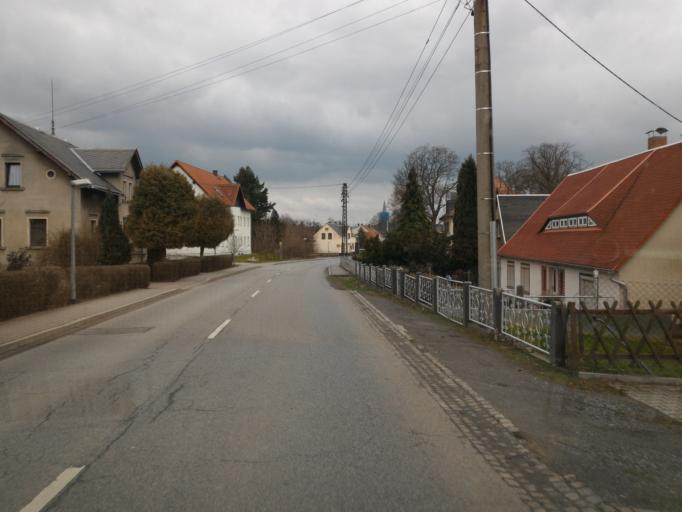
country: DE
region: Saxony
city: Leutersdorf
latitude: 50.9650
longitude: 14.6493
